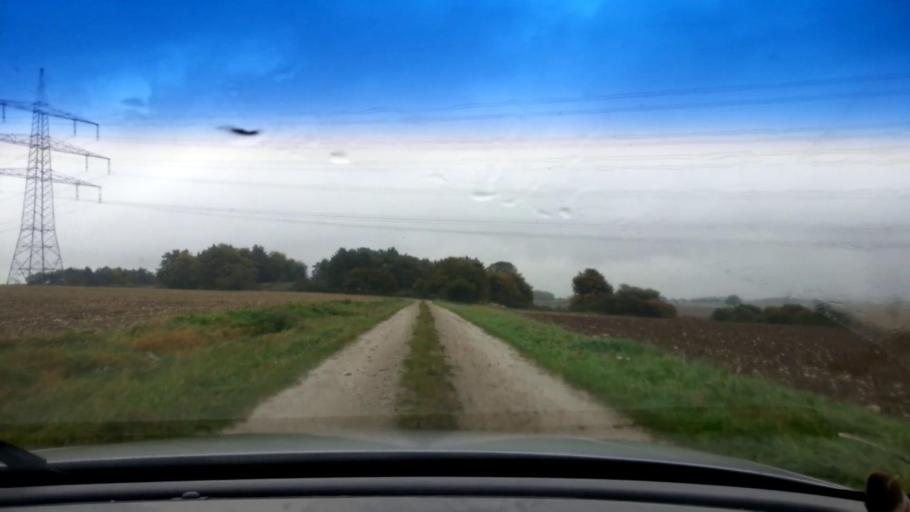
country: DE
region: Bavaria
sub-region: Upper Franconia
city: Wattendorf
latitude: 50.0353
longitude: 11.1297
